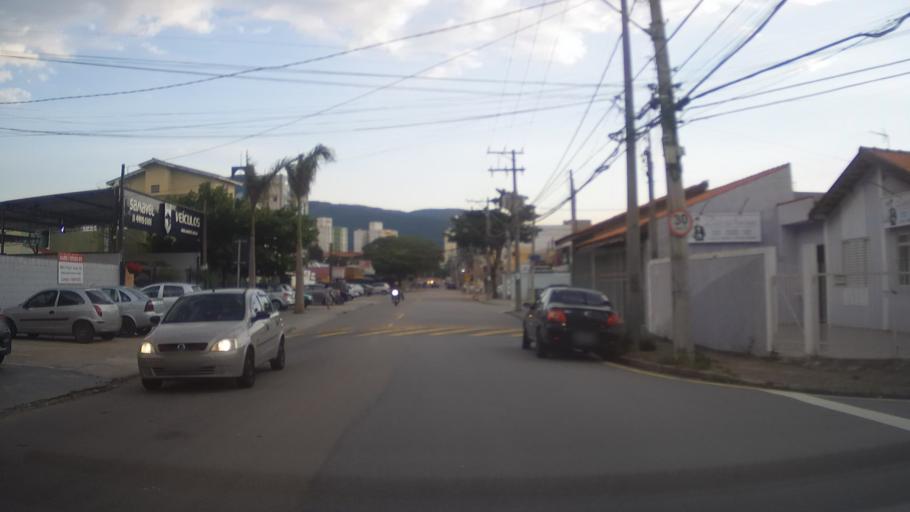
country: BR
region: Sao Paulo
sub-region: Jundiai
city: Jundiai
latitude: -23.1844
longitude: -46.9601
